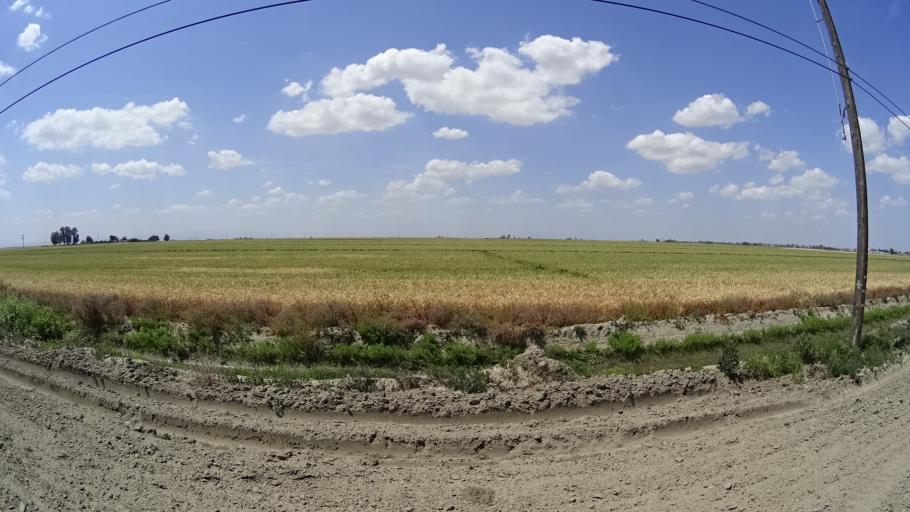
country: US
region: California
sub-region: Kings County
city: Stratford
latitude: 36.1700
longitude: -119.8161
